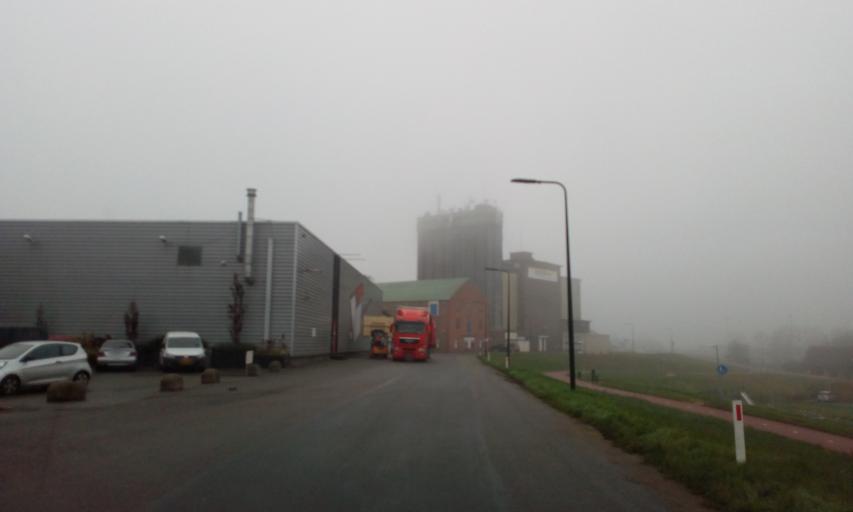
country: NL
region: South Holland
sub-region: Molenwaard
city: Liesveld
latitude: 51.9220
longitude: 4.7874
